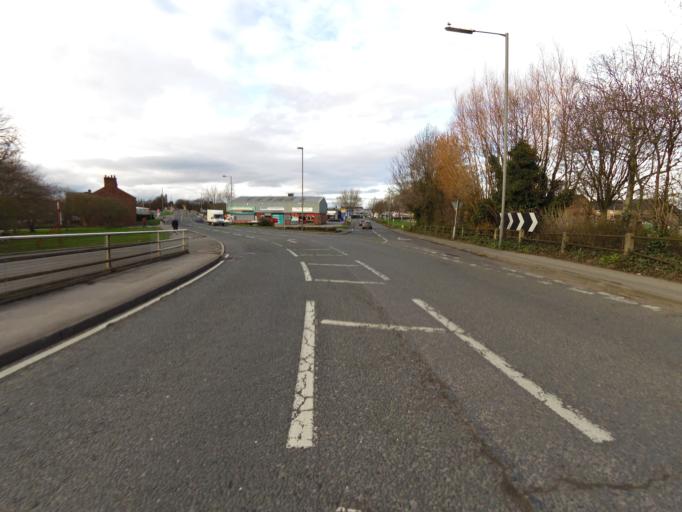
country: GB
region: England
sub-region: North Yorkshire
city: Selby
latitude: 53.7776
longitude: -1.0630
